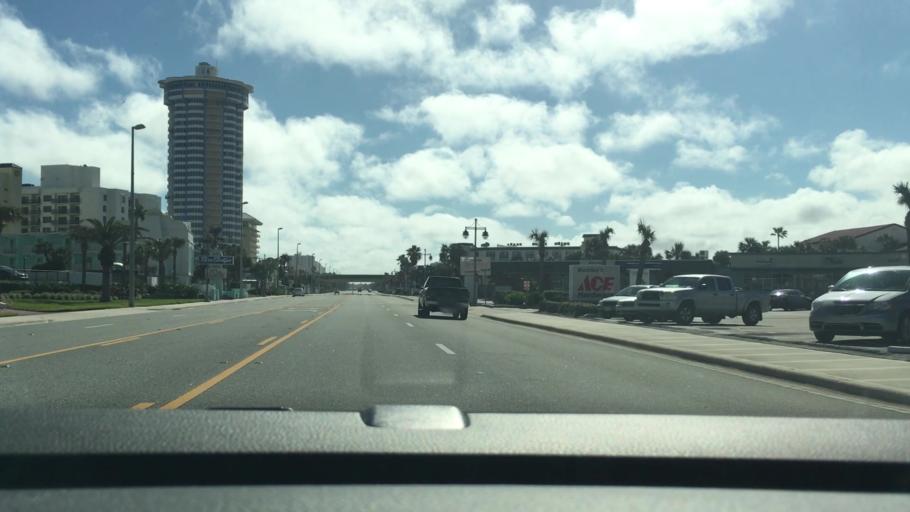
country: US
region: Florida
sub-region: Volusia County
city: Daytona Beach Shores
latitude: 29.1845
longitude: -80.9872
